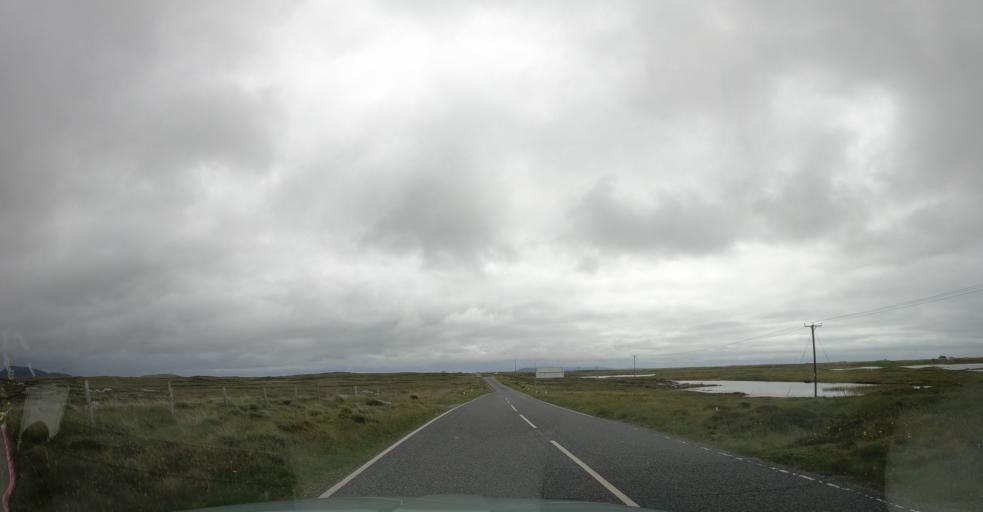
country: GB
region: Scotland
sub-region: Eilean Siar
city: Isle of North Uist
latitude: 57.5486
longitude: -7.3282
